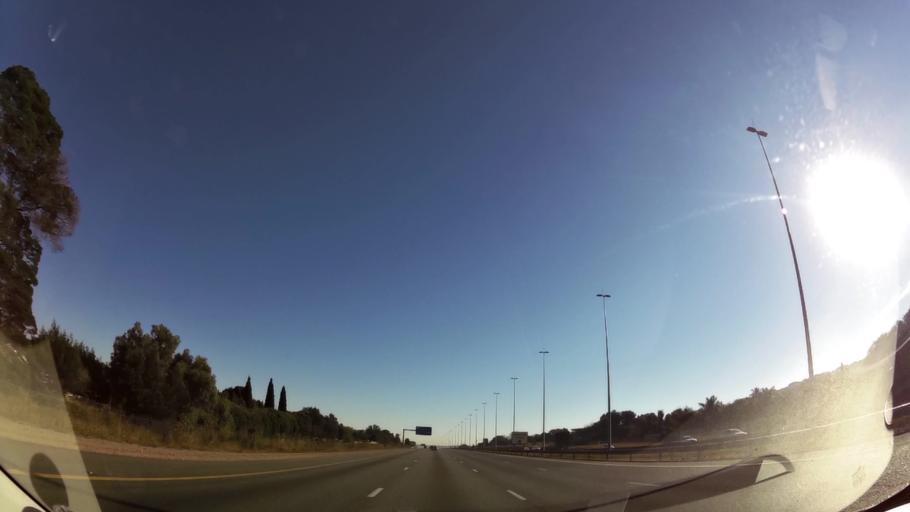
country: ZA
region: Gauteng
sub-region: City of Tshwane Metropolitan Municipality
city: Centurion
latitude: -25.8457
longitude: 28.2501
